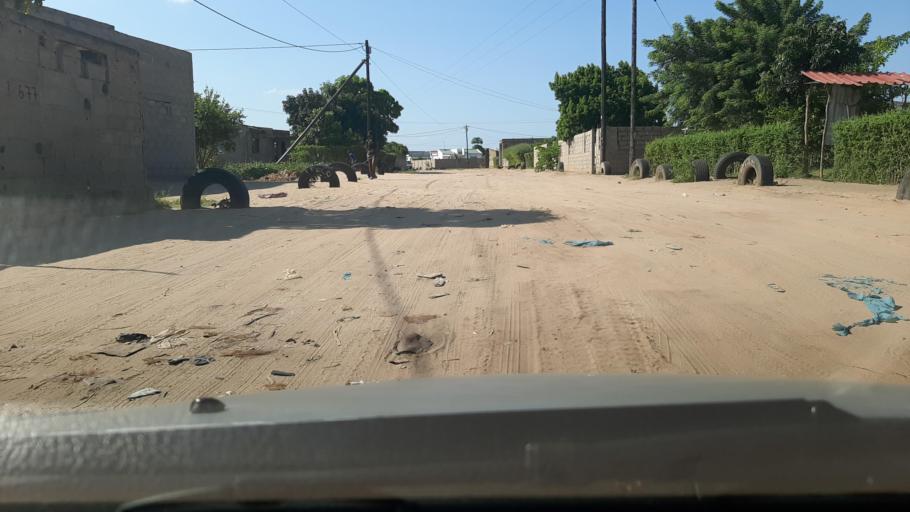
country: MZ
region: Maputo
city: Matola
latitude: -25.8097
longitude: 32.4919
